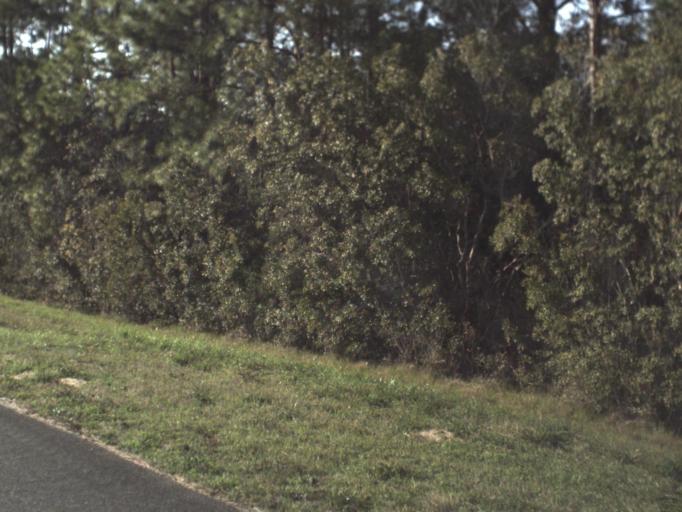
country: US
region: Florida
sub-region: Bay County
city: Lynn Haven
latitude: 30.4392
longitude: -85.7285
